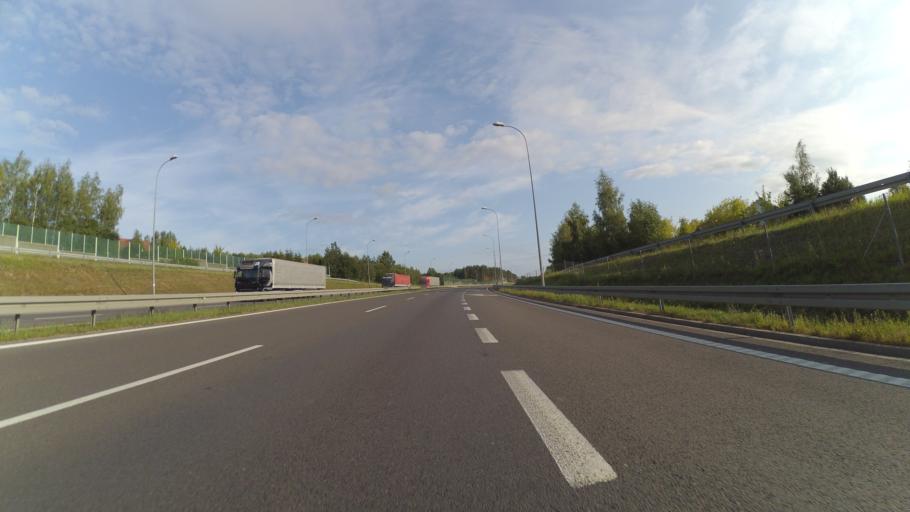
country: PL
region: Podlasie
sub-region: Powiat bialostocki
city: Wasilkow
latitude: 53.2017
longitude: 23.1541
